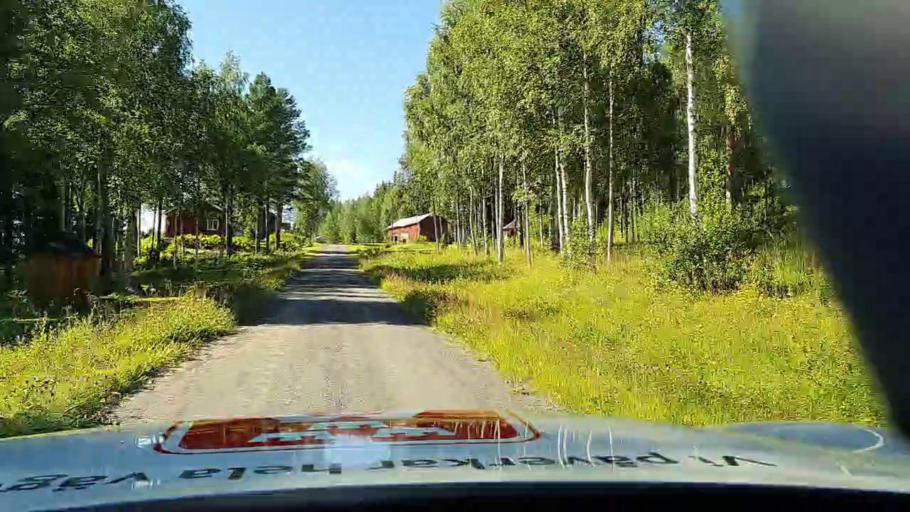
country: SE
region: Jaemtland
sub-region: OEstersunds Kommun
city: Lit
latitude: 63.7755
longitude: 14.6456
